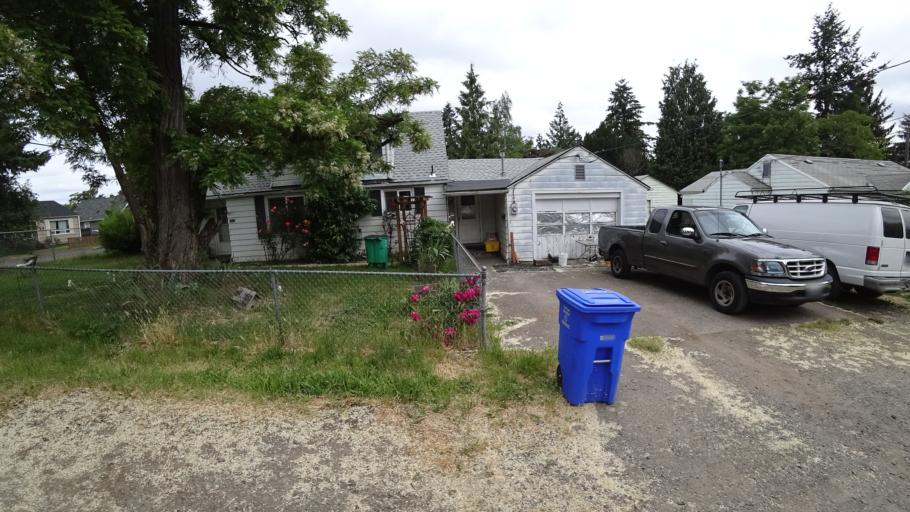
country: US
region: Oregon
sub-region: Multnomah County
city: Lents
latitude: 45.4745
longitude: -122.5852
